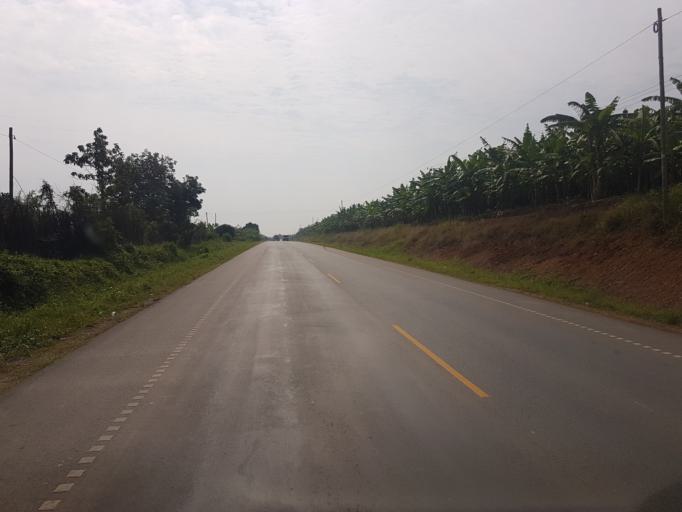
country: UG
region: Western Region
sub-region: Sheema District
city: Kibingo
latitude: -0.6377
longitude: 30.5141
